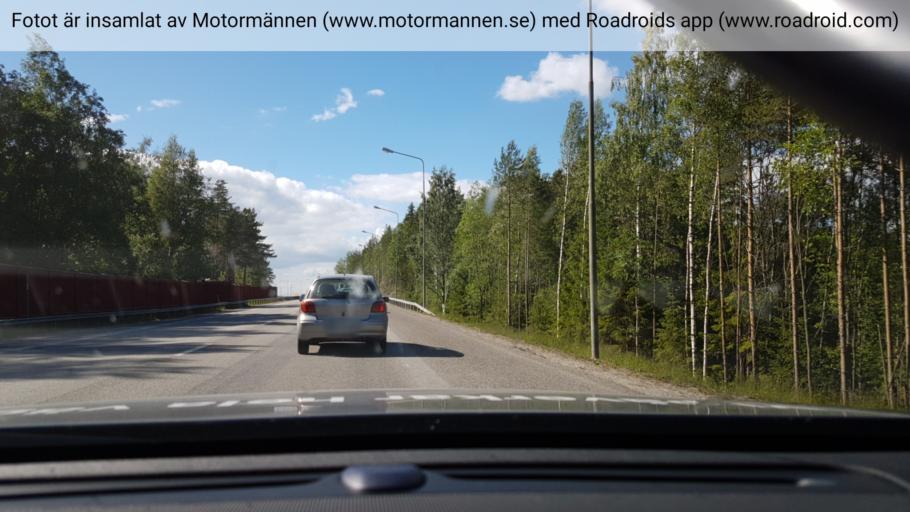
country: SE
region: Vaesterbotten
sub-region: Umea Kommun
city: Roback
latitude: 63.8379
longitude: 20.2129
